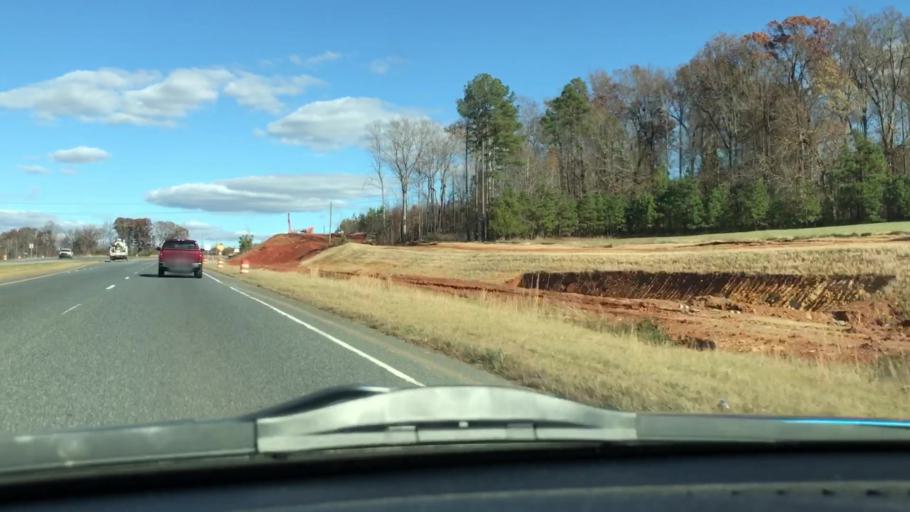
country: US
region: North Carolina
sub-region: Randolph County
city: Asheboro
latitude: 35.7216
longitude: -79.7555
